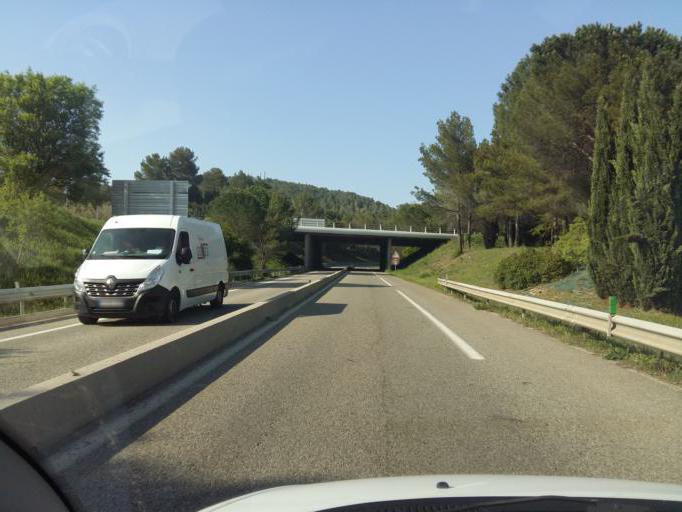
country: FR
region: Provence-Alpes-Cote d'Azur
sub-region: Departement du Var
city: Le Val
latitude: 43.4209
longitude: 6.0665
